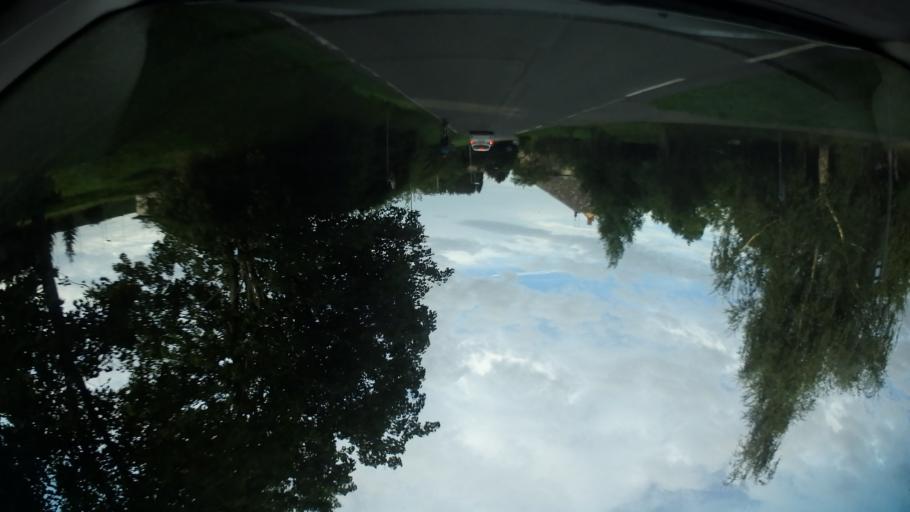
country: CZ
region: Olomoucky
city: Horni Stepanov
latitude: 49.5498
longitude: 16.7884
